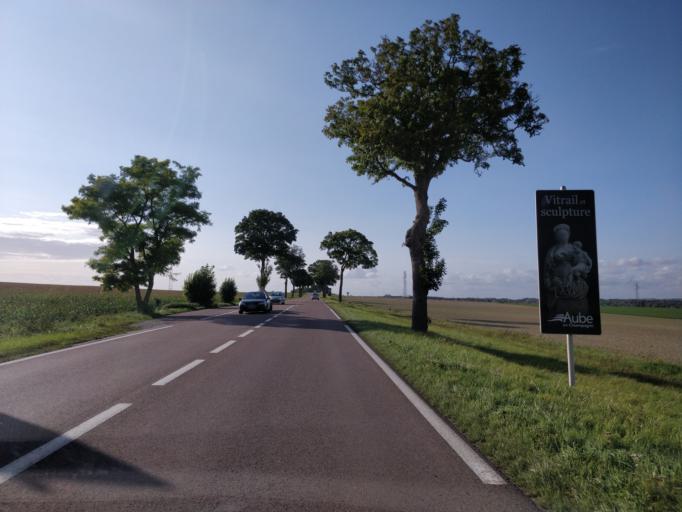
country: FR
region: Champagne-Ardenne
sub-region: Departement de l'Aube
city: Saint-Parres-aux-Tertres
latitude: 48.2887
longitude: 4.1582
